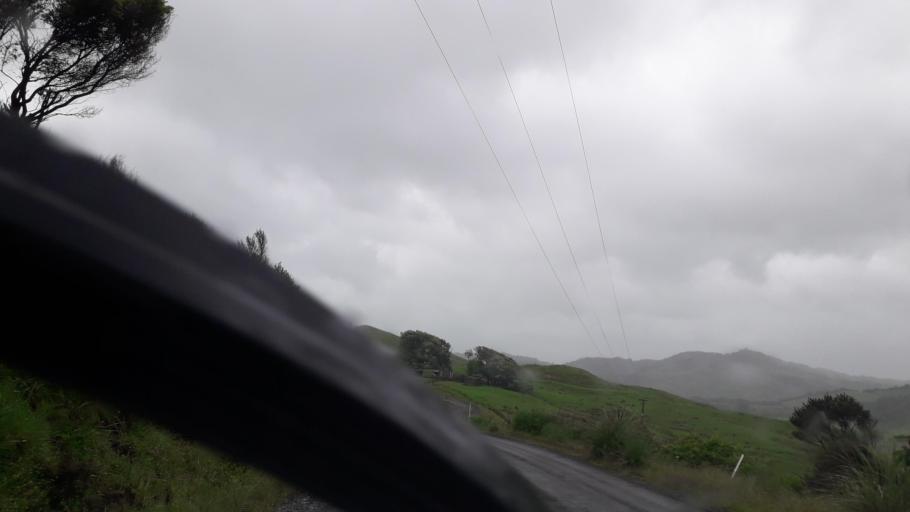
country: NZ
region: Northland
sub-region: Far North District
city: Kaitaia
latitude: -35.4130
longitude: 173.3657
